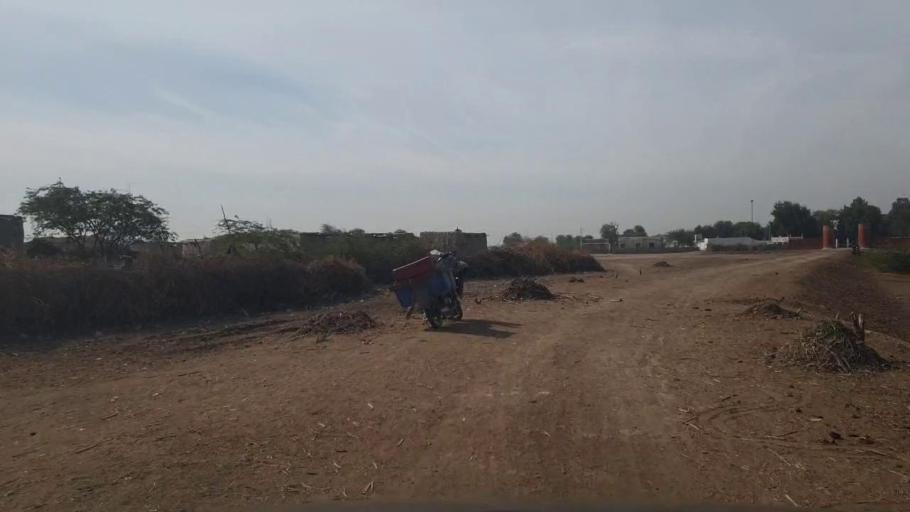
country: PK
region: Sindh
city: Umarkot
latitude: 25.3576
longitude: 69.6659
